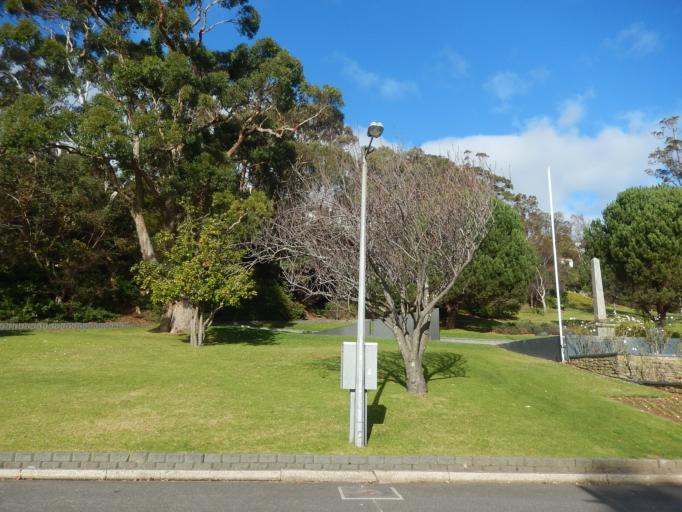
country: AU
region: Tasmania
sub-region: Burnie
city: Burnie
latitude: -41.0472
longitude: 145.8971
